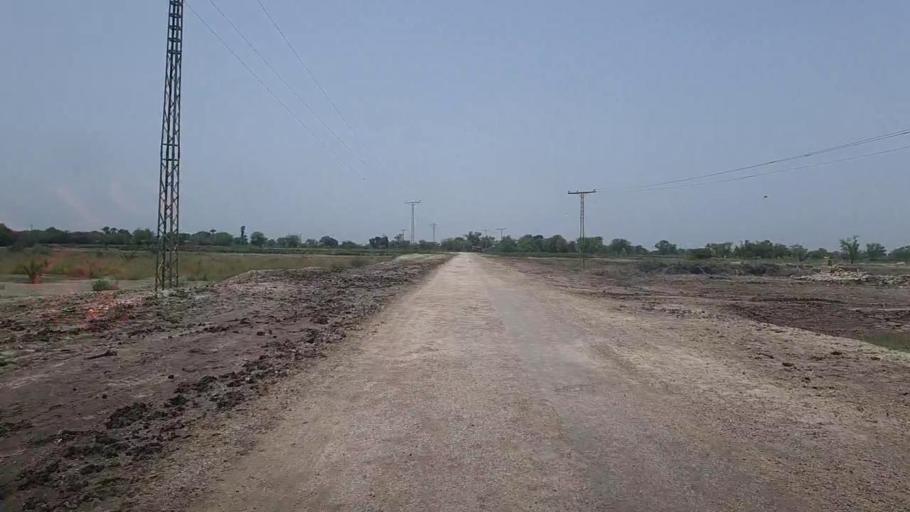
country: PK
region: Sindh
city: Pad Idan
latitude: 26.8343
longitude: 68.3120
